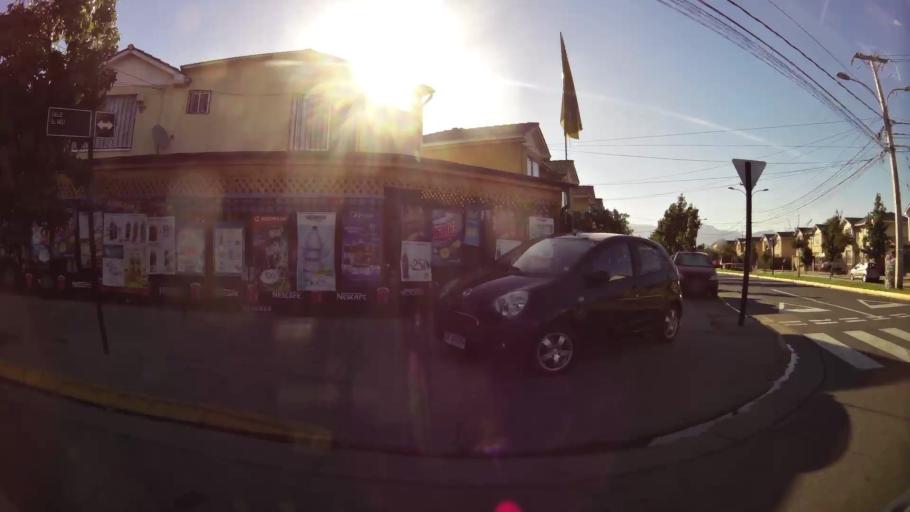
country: CL
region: O'Higgins
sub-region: Provincia de Cachapoal
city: Rancagua
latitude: -34.1833
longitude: -70.7603
